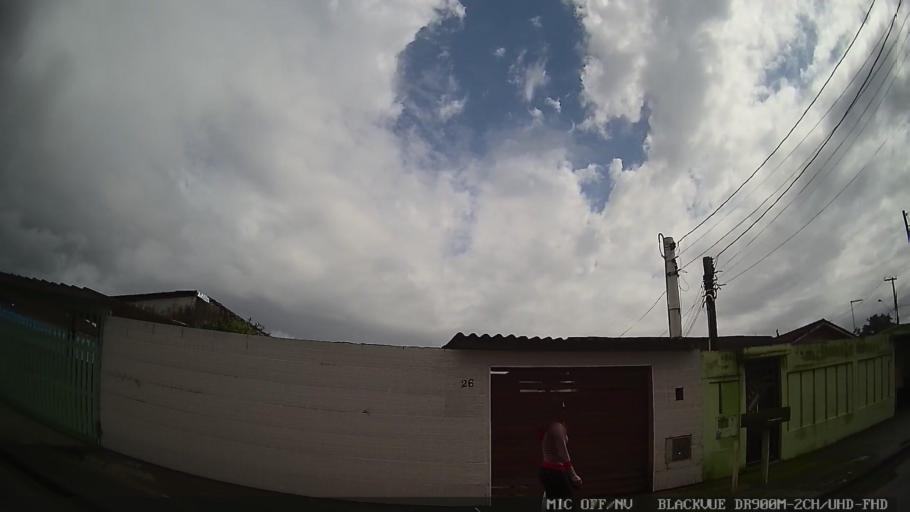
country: BR
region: Sao Paulo
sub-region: Itanhaem
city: Itanhaem
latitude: -24.1891
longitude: -46.8120
